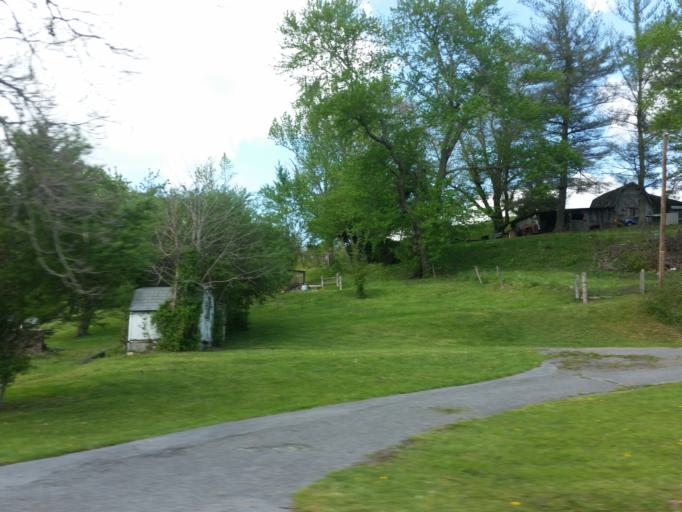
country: US
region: Kentucky
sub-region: Bell County
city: Middlesboro
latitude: 36.6321
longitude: -83.7220
